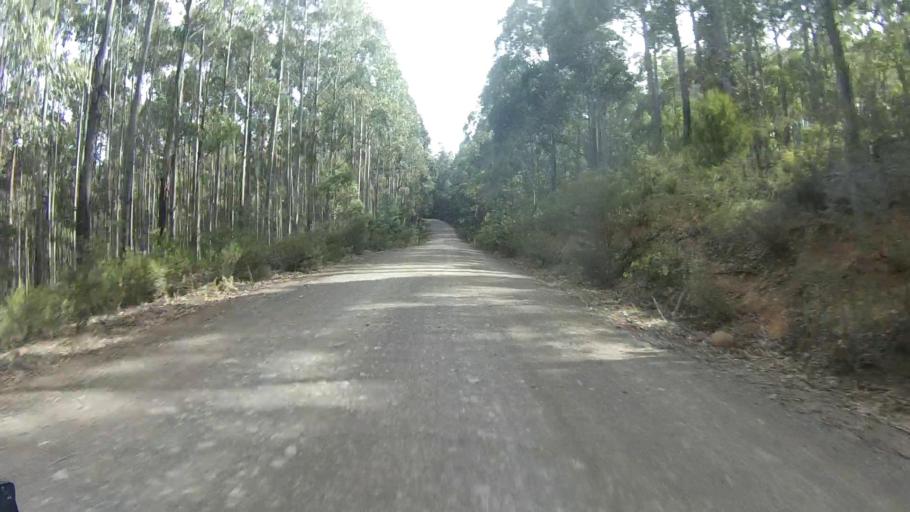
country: AU
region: Tasmania
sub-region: Sorell
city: Sorell
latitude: -42.7489
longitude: 147.8287
